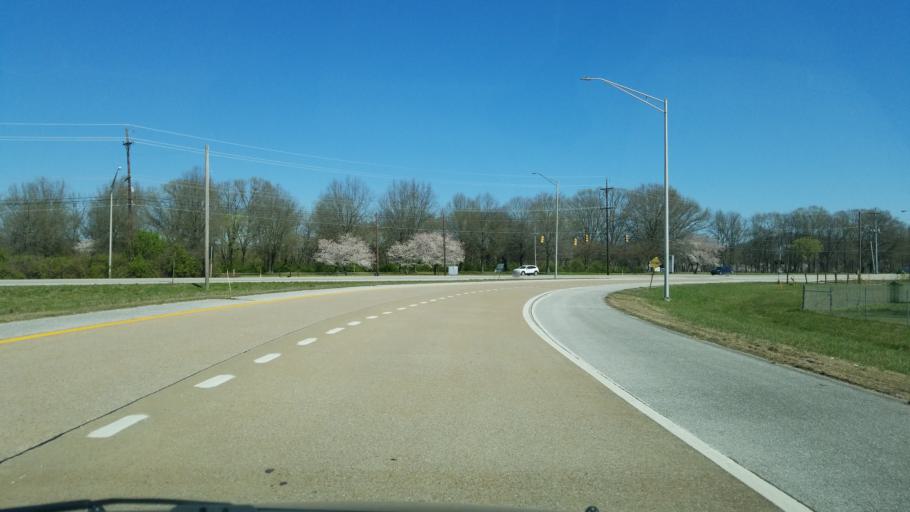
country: US
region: Tennessee
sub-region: Hamilton County
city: East Chattanooga
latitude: 35.0950
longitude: -85.2458
